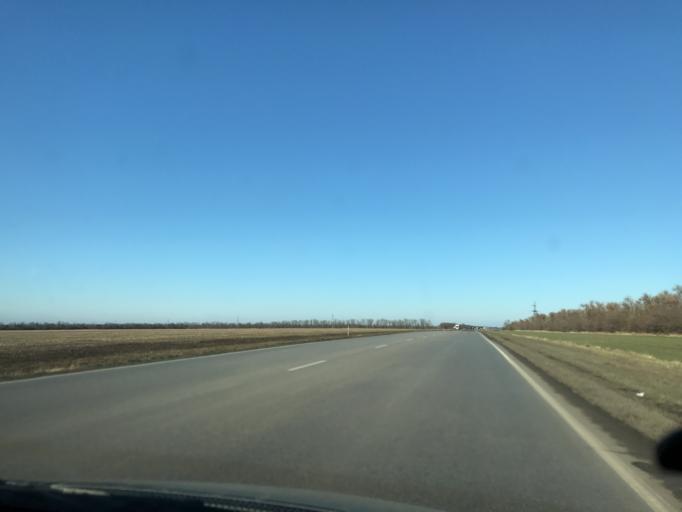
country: RU
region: Rostov
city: Kagal'nitskaya
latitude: 46.9233
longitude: 40.1024
